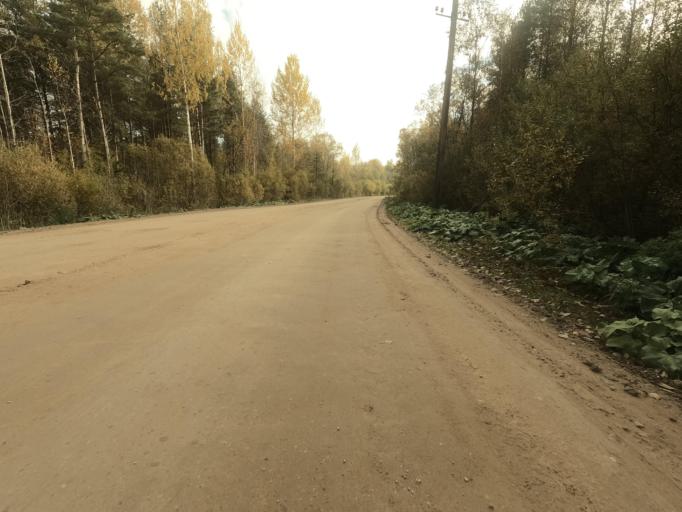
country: RU
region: Novgorod
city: Batetskiy
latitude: 58.8026
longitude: 30.6466
